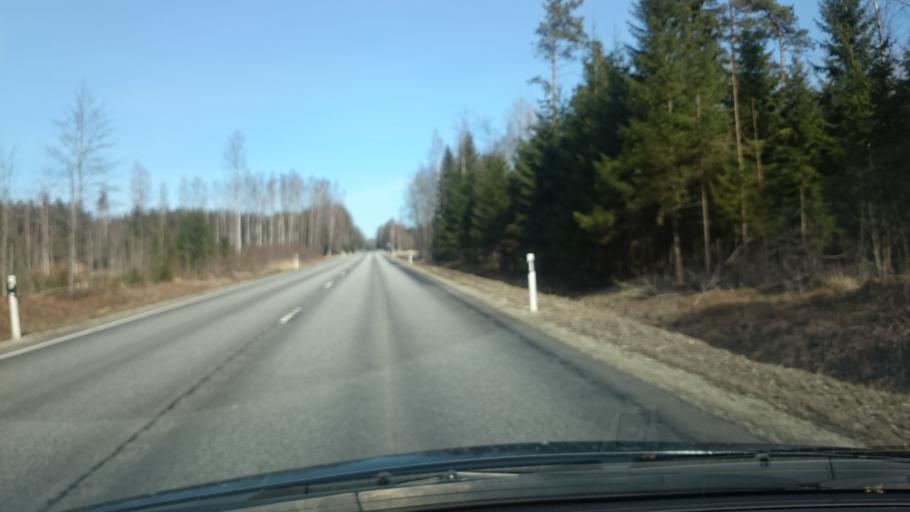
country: EE
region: Jaervamaa
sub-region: Tueri vald
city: Sarevere
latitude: 58.7054
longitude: 25.2642
